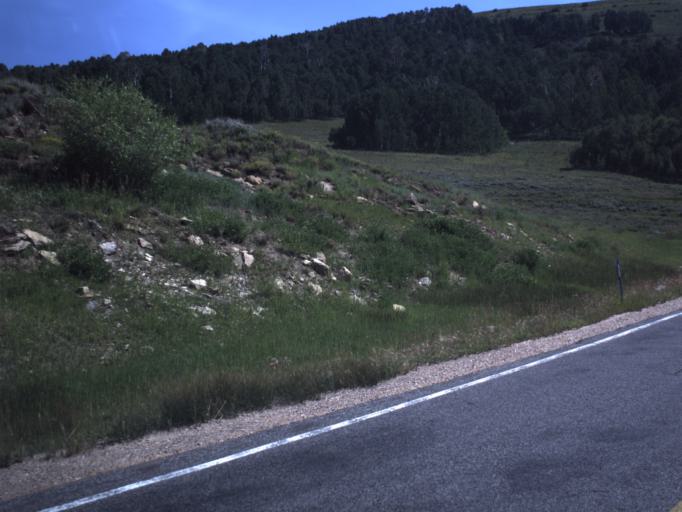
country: US
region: Utah
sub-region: Sanpete County
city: Fairview
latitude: 39.6555
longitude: -111.2958
